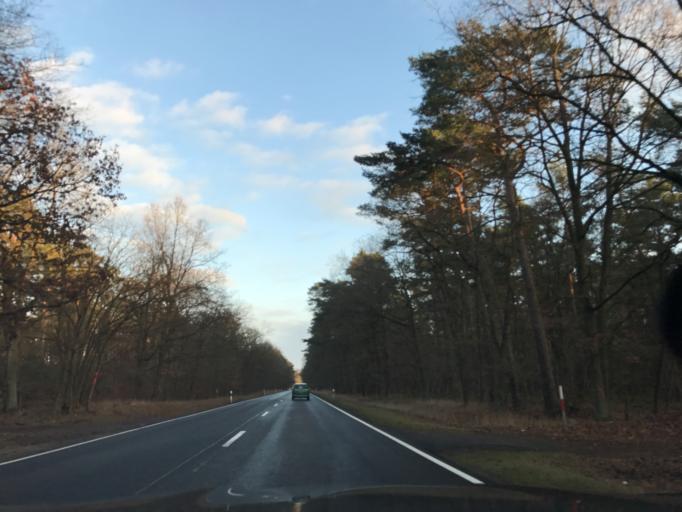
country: DE
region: Brandenburg
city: Bensdorf
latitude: 52.4111
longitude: 12.2892
